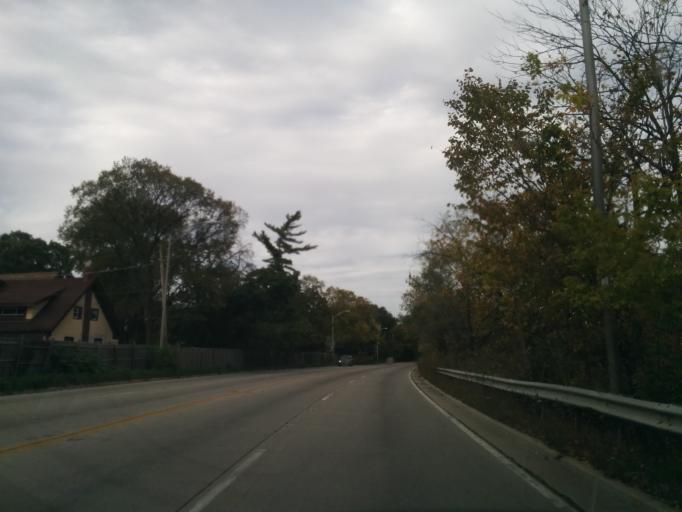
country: US
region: Illinois
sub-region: Cook County
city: Maywood
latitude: 41.8953
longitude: -87.8350
